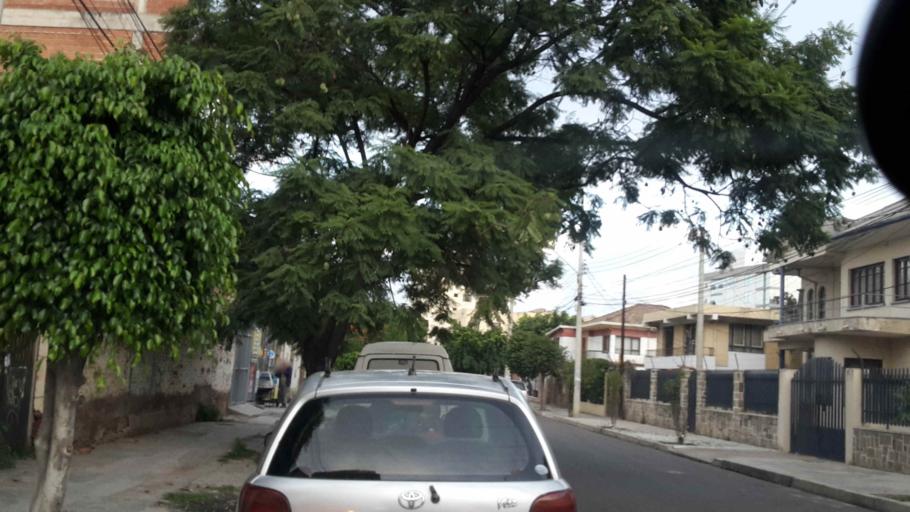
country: BO
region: Cochabamba
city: Cochabamba
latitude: -17.3819
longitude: -66.1550
